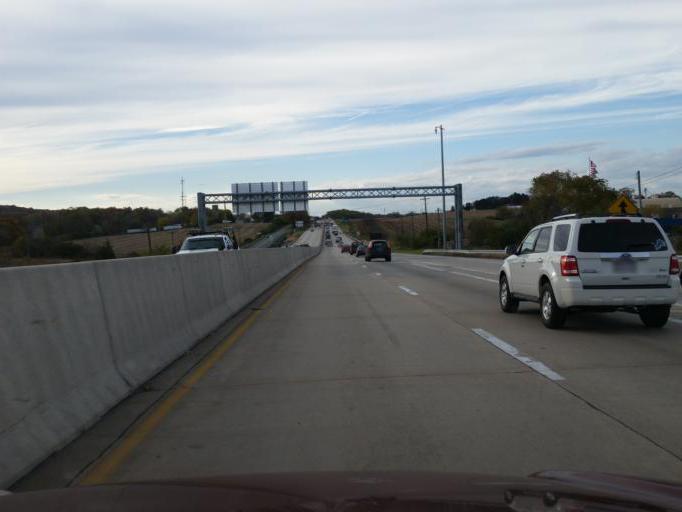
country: US
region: Pennsylvania
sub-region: Lancaster County
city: East Petersburg
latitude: 40.0818
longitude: -76.3551
